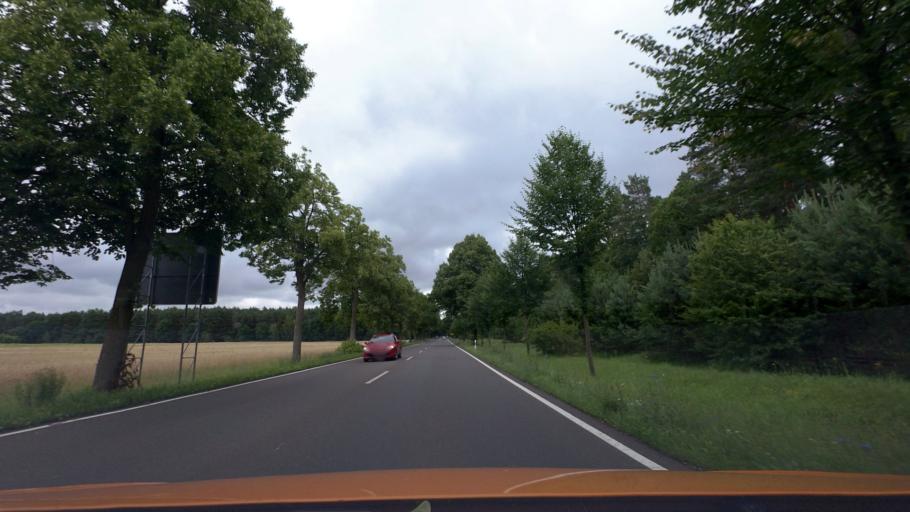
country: DE
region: Brandenburg
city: Werftpfuhl
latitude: 52.6609
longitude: 13.7954
